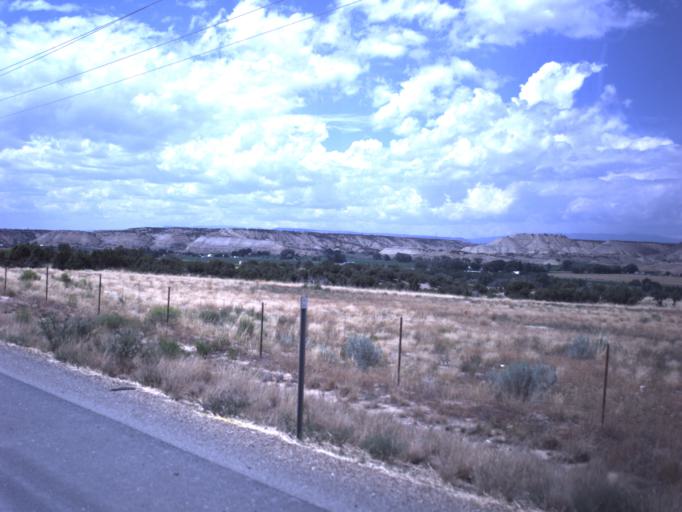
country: US
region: Utah
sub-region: Duchesne County
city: Duchesne
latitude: 40.1720
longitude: -110.3382
